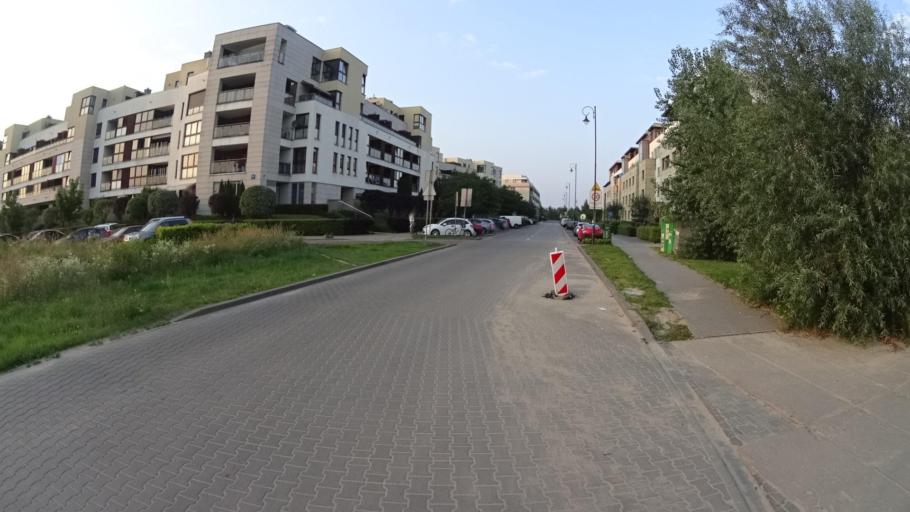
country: PL
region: Masovian Voivodeship
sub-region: Warszawa
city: Wilanow
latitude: 52.1550
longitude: 21.0807
